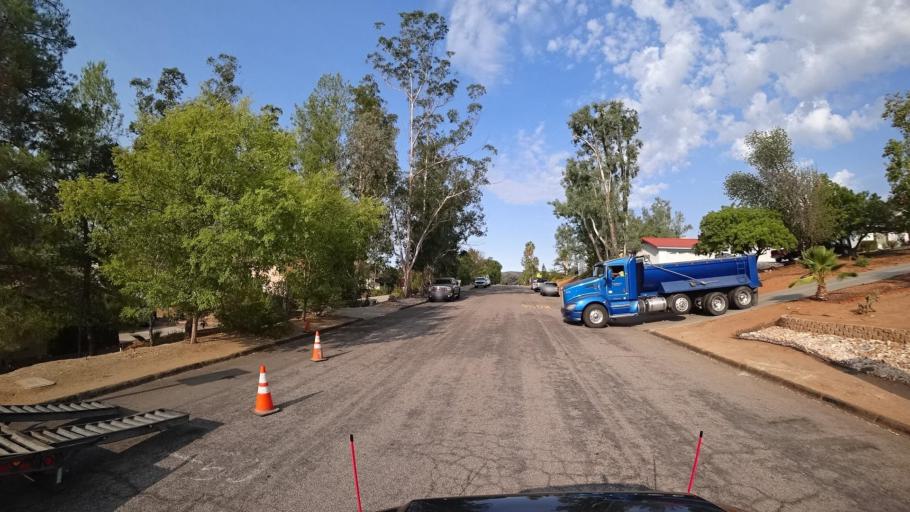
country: US
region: California
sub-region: San Diego County
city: San Diego Country Estates
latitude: 33.0078
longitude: -116.7899
